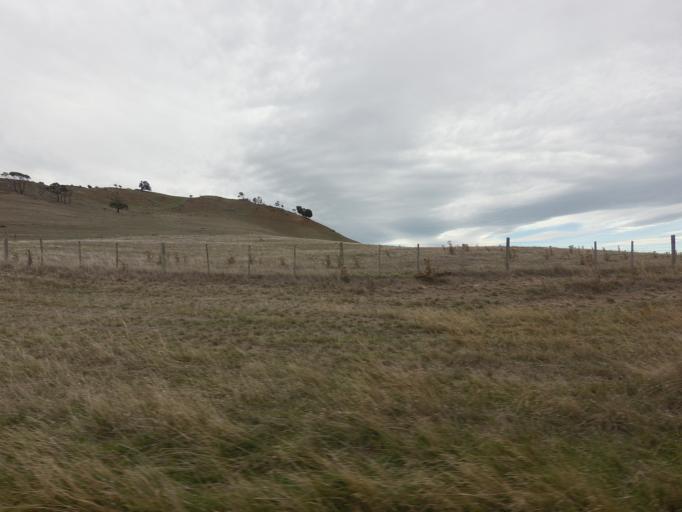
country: AU
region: Tasmania
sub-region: Derwent Valley
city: New Norfolk
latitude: -42.3715
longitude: 146.8533
